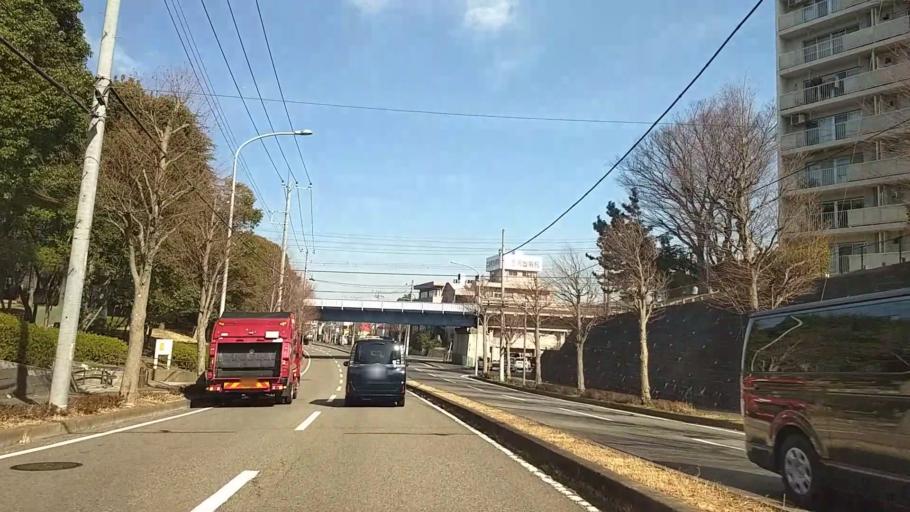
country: JP
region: Kanagawa
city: Kamakura
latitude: 35.3751
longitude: 139.5818
